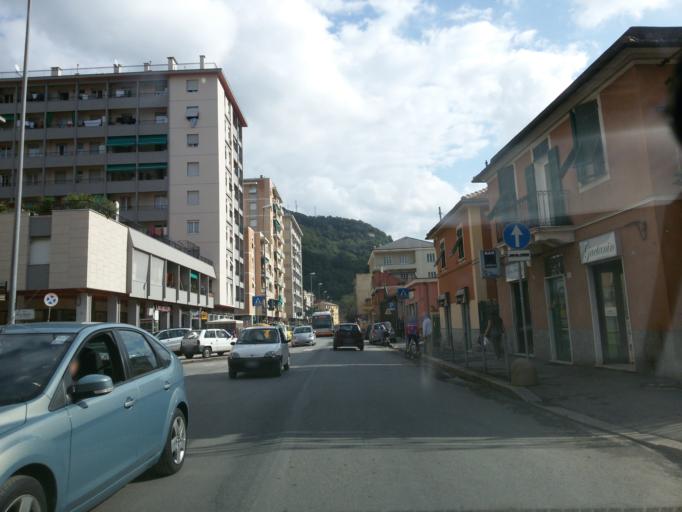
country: IT
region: Liguria
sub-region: Provincia di Genova
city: Piccarello
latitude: 44.4543
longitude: 8.9809
